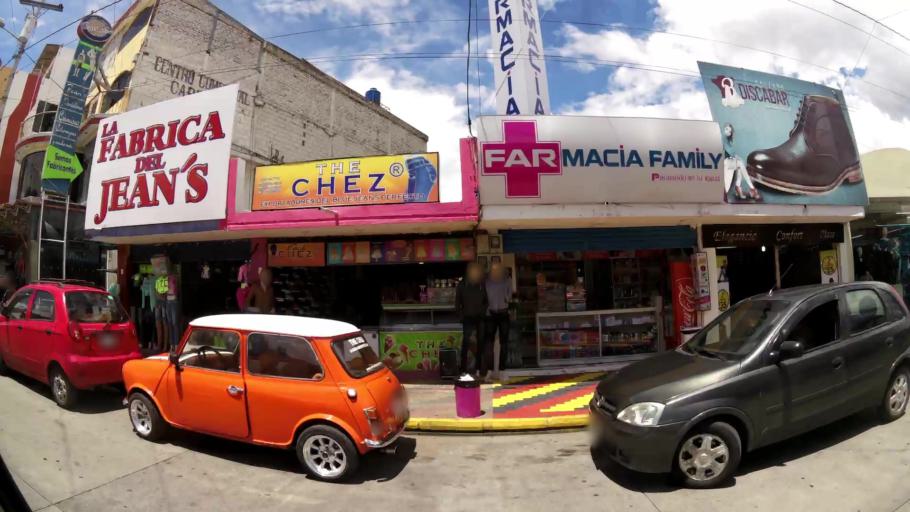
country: EC
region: Tungurahua
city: Pelileo
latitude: -1.3323
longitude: -78.5518
